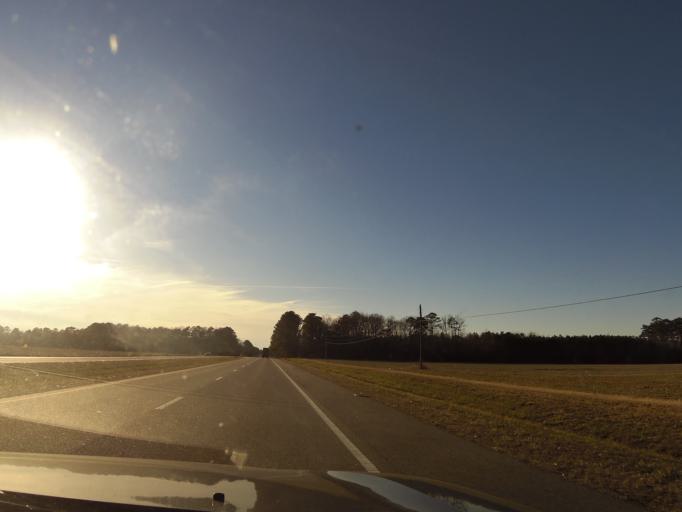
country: US
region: Virginia
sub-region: City of Franklin
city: Franklin
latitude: 36.6538
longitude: -76.8285
